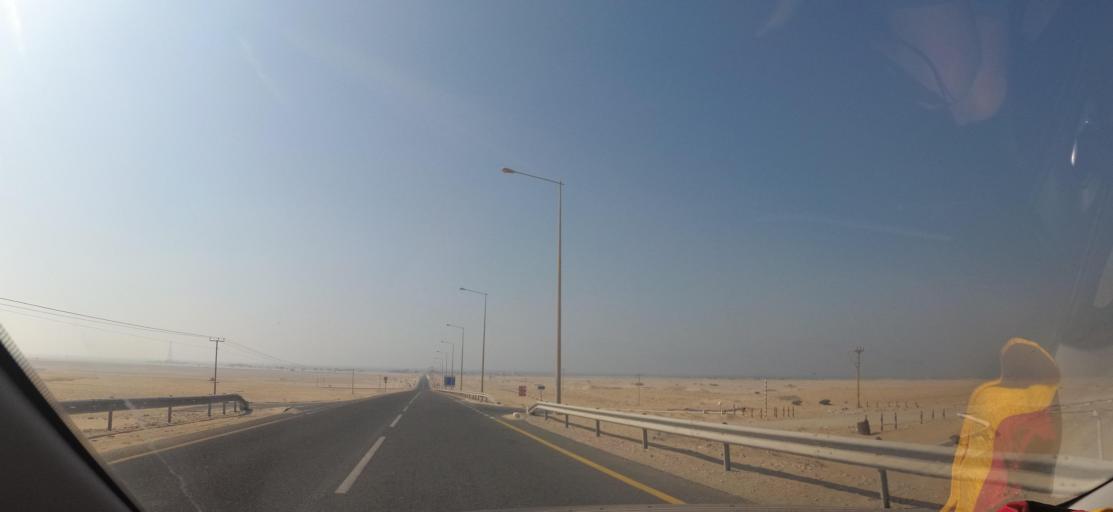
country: QA
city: Umm Bab
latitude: 25.2120
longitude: 50.7849
